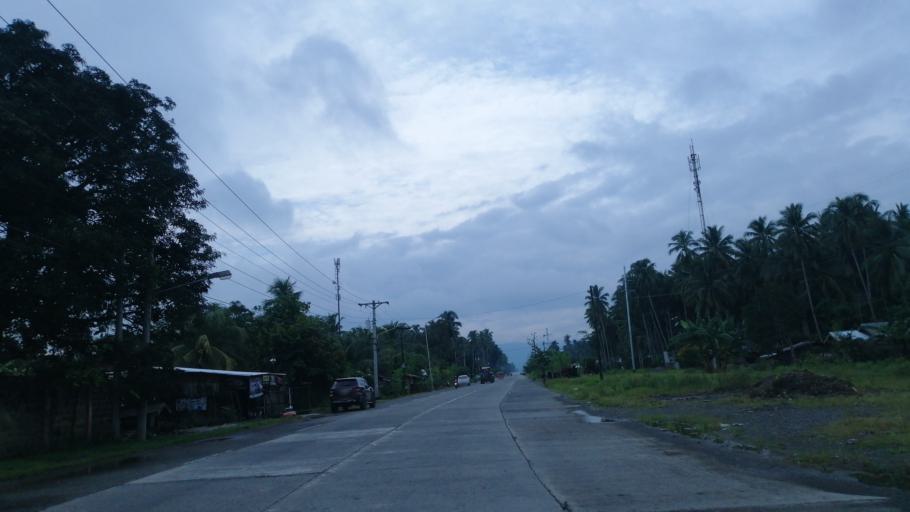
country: PH
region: Davao
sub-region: Province of Davao del Norte
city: Corocotan
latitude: 7.3990
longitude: 125.7736
